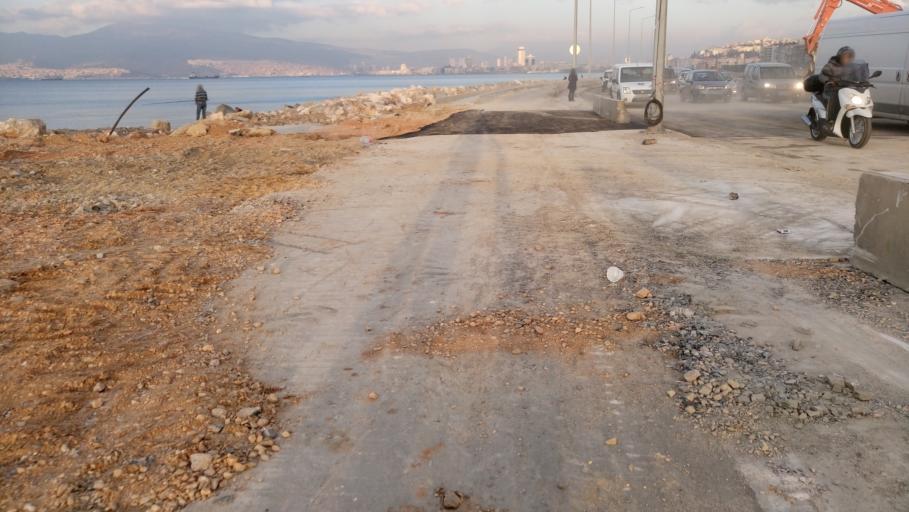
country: TR
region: Izmir
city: Izmir
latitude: 38.4074
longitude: 27.1016
